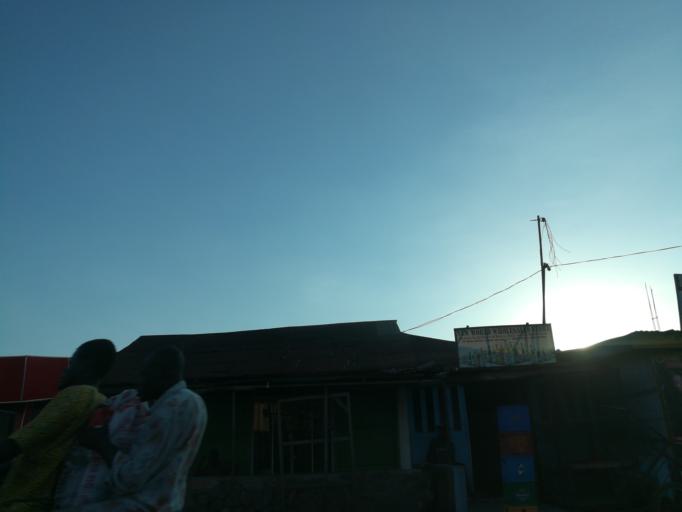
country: NG
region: Lagos
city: Ikorodu
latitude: 6.6163
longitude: 3.5094
